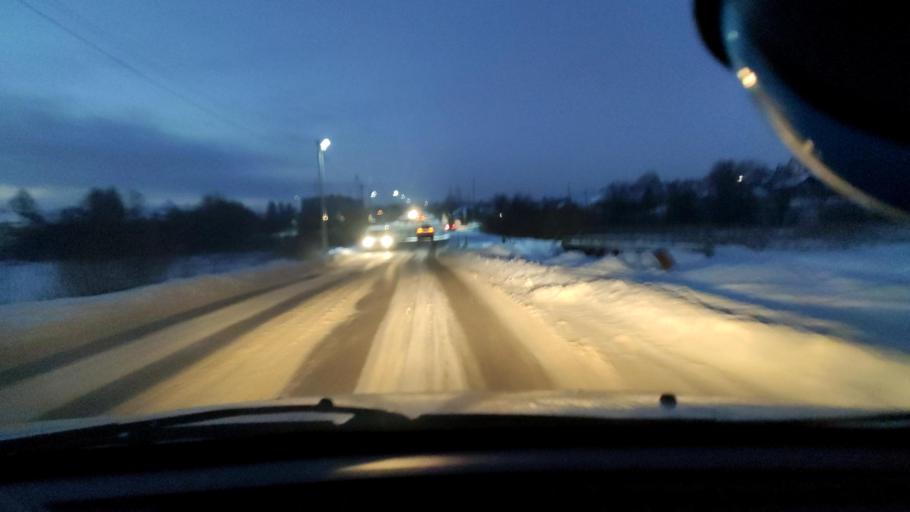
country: RU
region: Perm
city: Kultayevo
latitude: 57.8990
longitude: 55.9273
